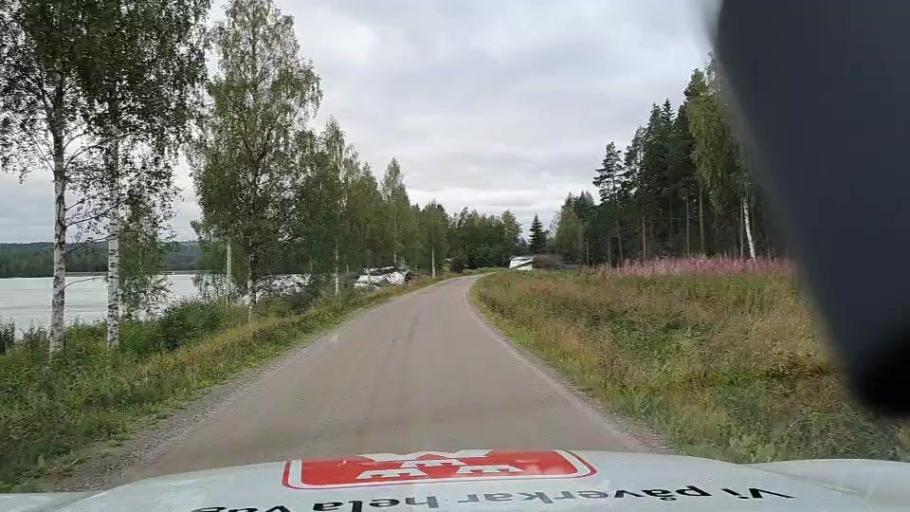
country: SE
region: Jaemtland
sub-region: Ragunda Kommun
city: Hammarstrand
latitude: 63.1689
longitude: 15.8264
